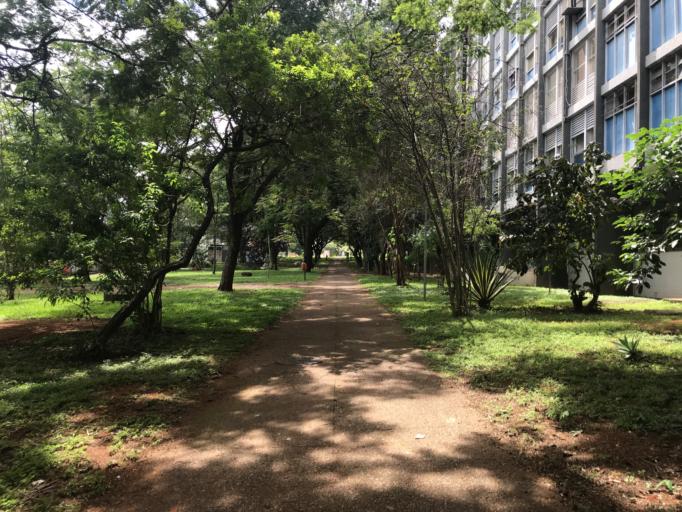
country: BR
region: Federal District
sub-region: Brasilia
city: Brasilia
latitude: -15.8191
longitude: -47.9075
